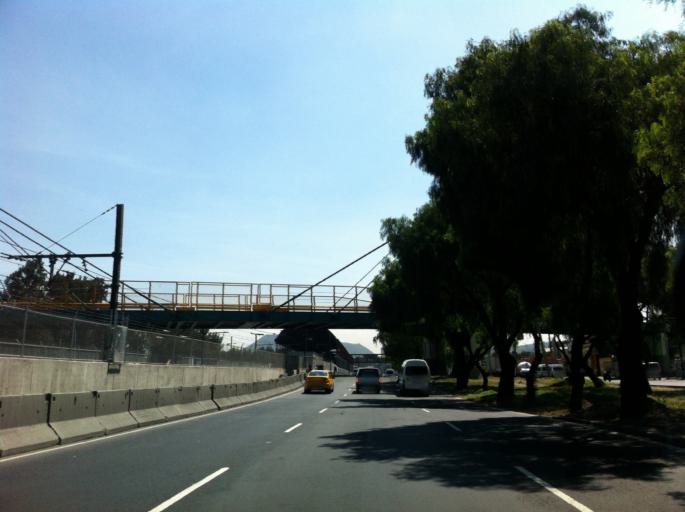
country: MX
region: Mexico
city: Los Reyes La Paz
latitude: 19.3667
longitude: -99.0084
